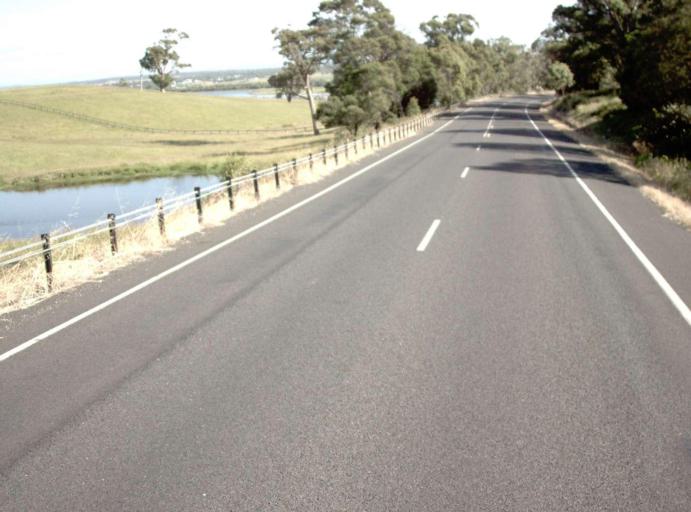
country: AU
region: Victoria
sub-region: East Gippsland
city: Lakes Entrance
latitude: -37.8554
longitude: 147.8452
